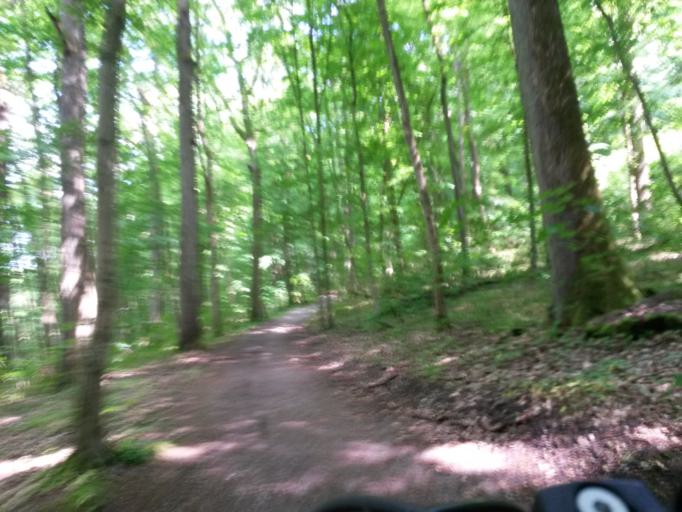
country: DE
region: Bavaria
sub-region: Regierungsbezirk Unterfranken
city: Bad Kissingen
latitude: 50.1740
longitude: 10.0704
